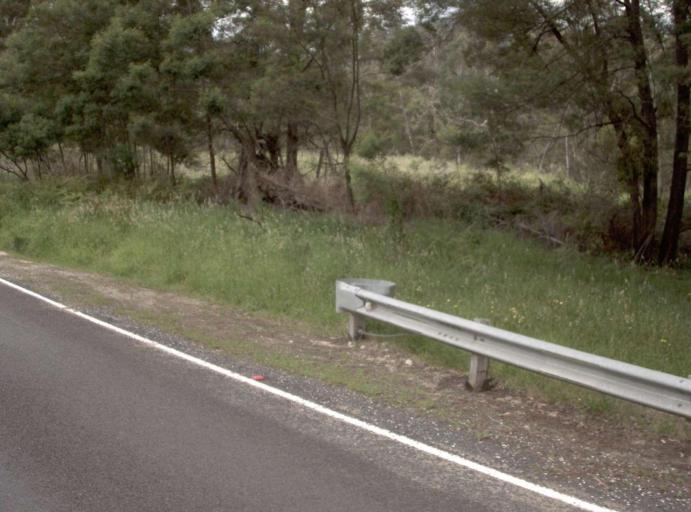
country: AU
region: New South Wales
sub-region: Bombala
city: Bombala
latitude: -37.4323
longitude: 149.1981
